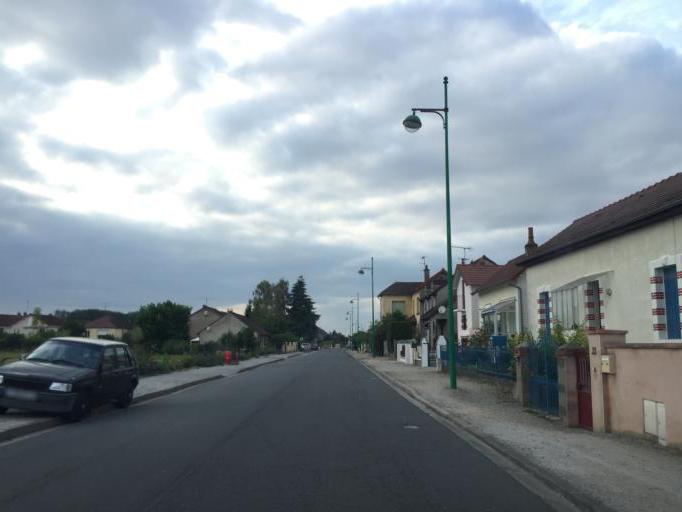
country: FR
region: Auvergne
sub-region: Departement de l'Allier
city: Yzeure
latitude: 46.5576
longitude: 3.3587
